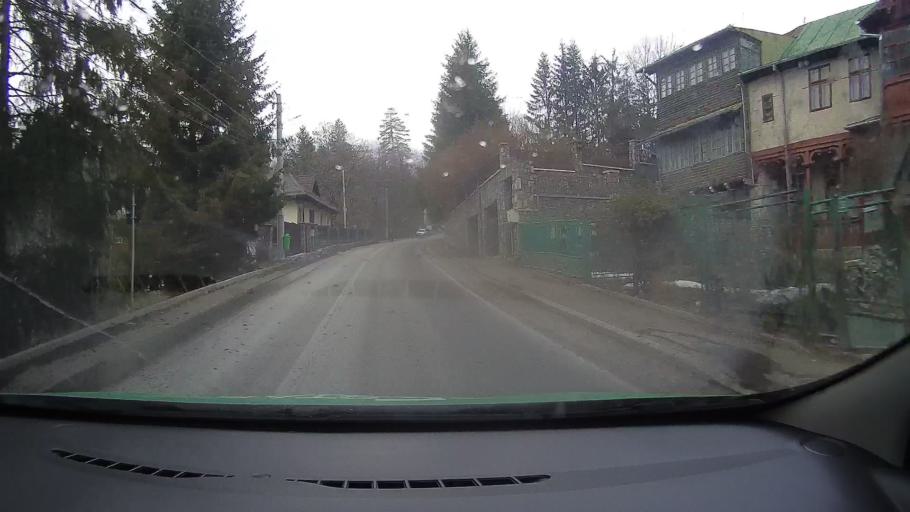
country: RO
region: Prahova
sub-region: Oras Sinaia
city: Sinaia
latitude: 45.3540
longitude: 25.5436
